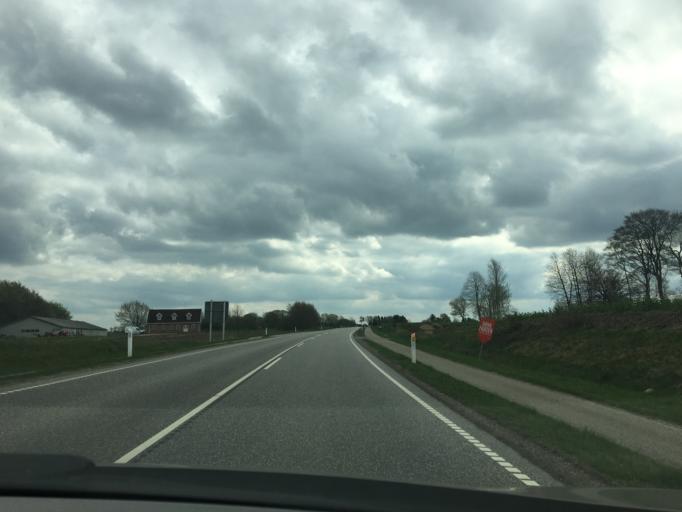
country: DK
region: Central Jutland
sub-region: Horsens Kommune
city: Braedstrup
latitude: 56.0323
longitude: 9.6111
